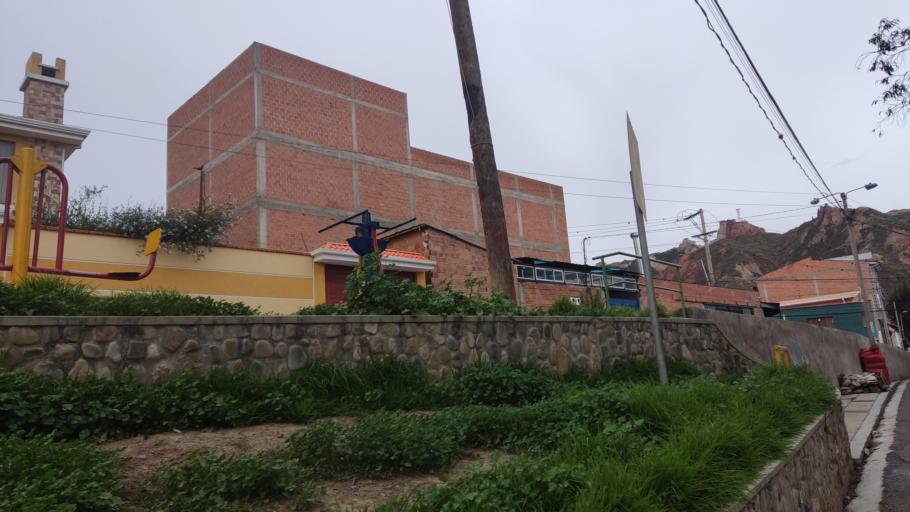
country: BO
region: La Paz
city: La Paz
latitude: -16.5682
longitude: -68.0885
